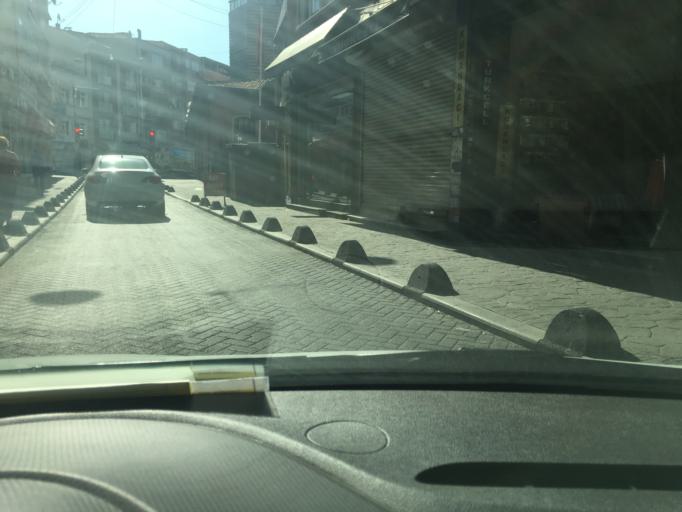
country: TR
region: Istanbul
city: Eminoenue
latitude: 41.0355
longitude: 28.9678
